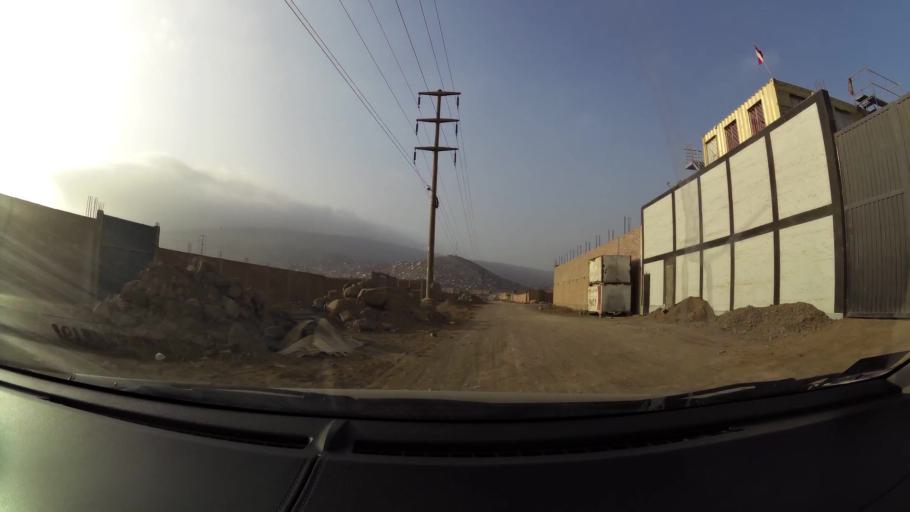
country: PE
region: Lima
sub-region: Lima
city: Santa Rosa
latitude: -11.7520
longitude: -77.1507
